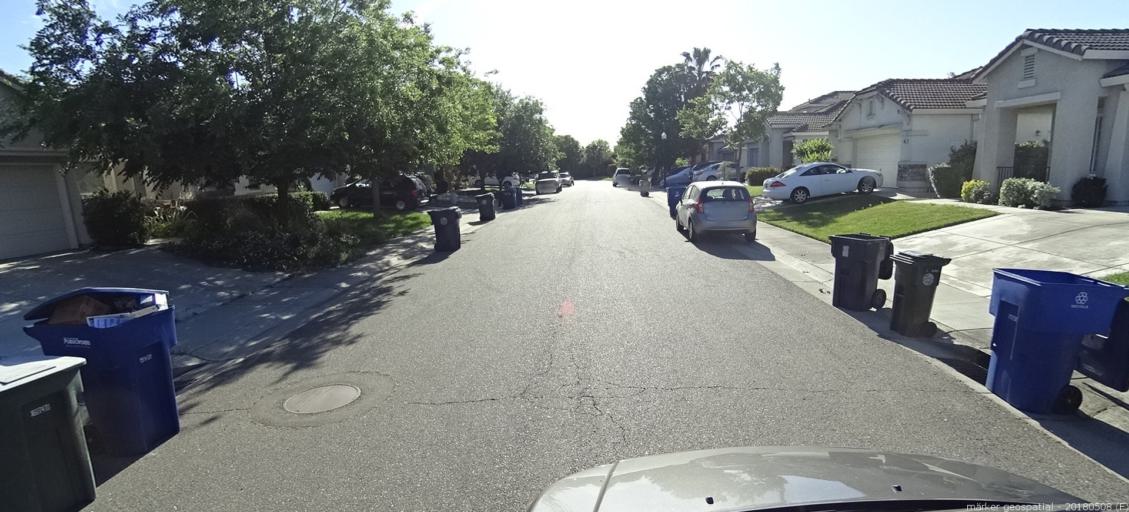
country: US
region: California
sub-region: Sacramento County
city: Elverta
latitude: 38.6800
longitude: -121.5065
